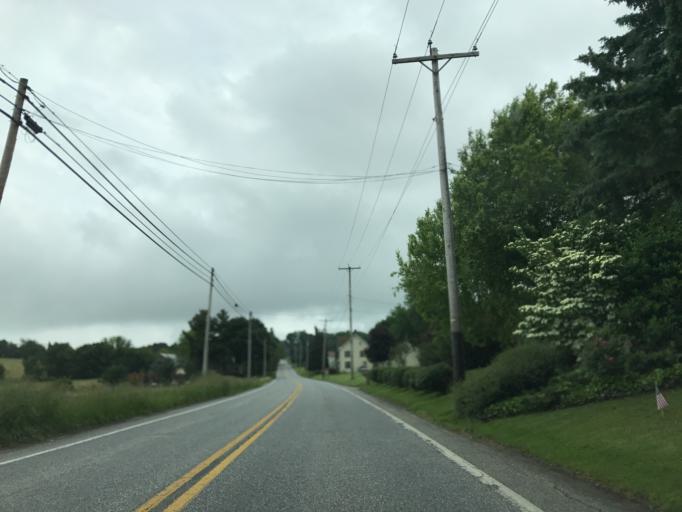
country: US
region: Pennsylvania
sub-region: York County
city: Red Lion
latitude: 39.8321
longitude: -76.6172
